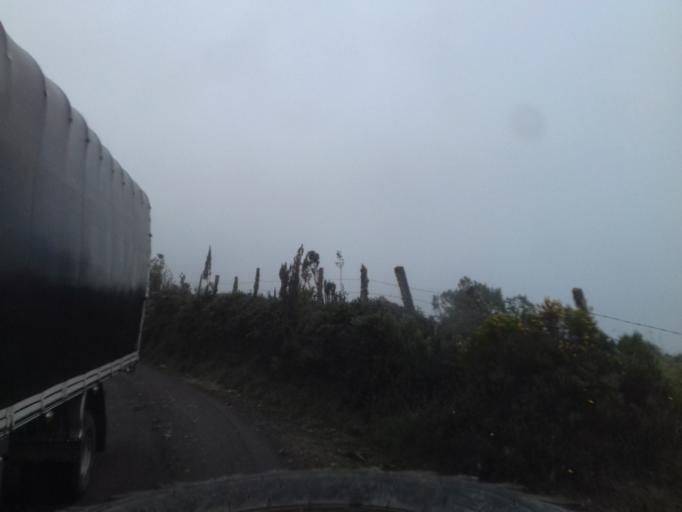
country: CO
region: Tolima
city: Murillo
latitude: 4.9011
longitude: -75.2522
